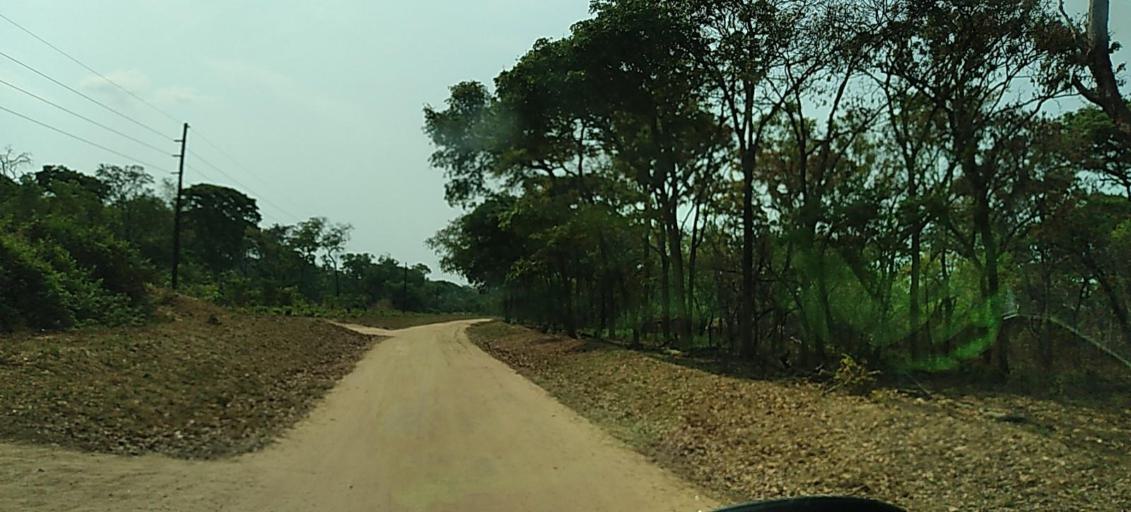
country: ZM
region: North-Western
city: Solwezi
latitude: -12.7061
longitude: 26.4175
